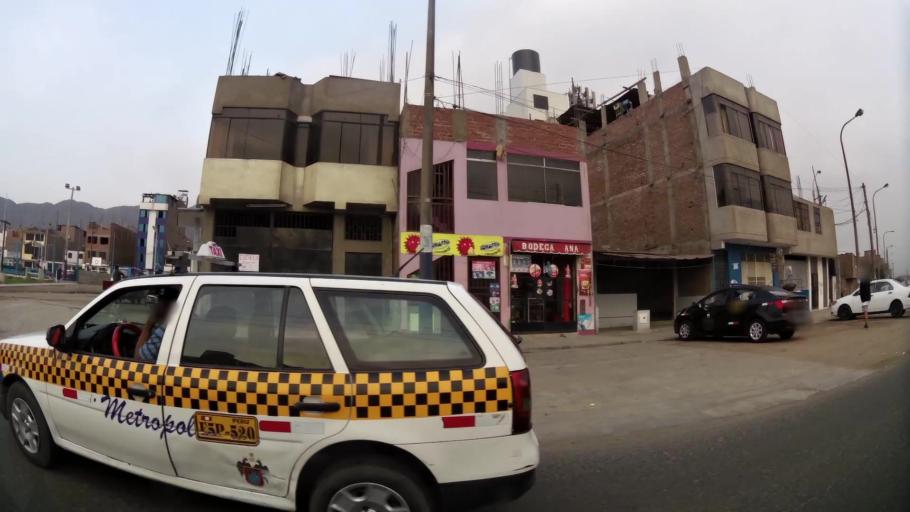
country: PE
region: Lima
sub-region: Lima
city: Independencia
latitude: -11.9925
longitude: -77.0006
